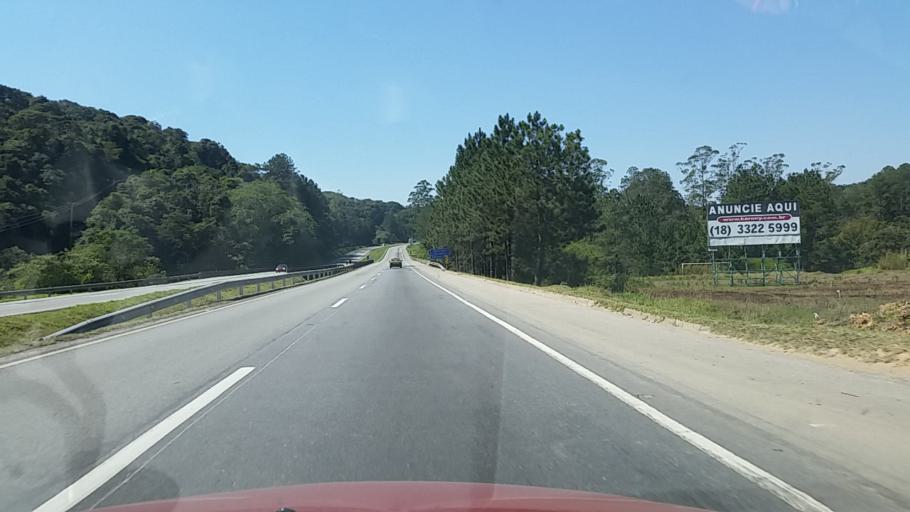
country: BR
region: Sao Paulo
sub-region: Juquitiba
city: Juquitiba
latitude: -23.9412
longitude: -47.0914
